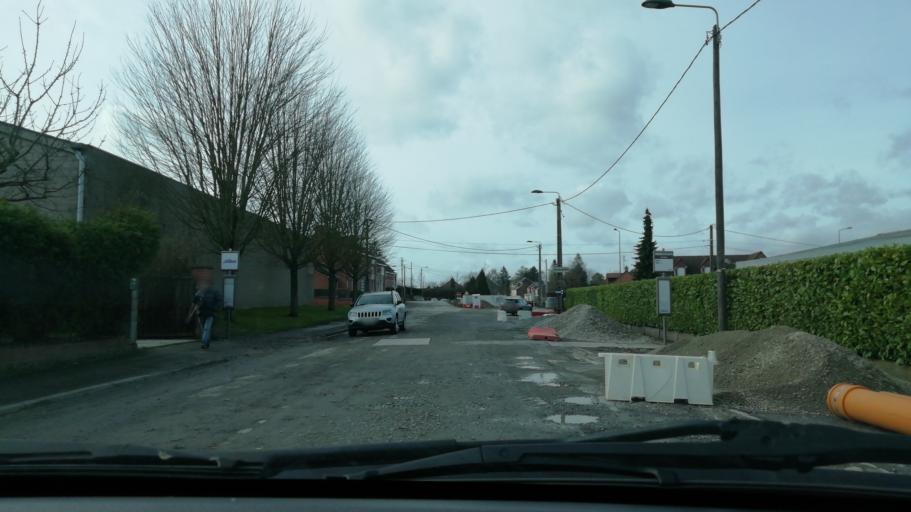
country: FR
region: Nord-Pas-de-Calais
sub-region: Departement du Nord
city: Louvroil
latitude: 50.2784
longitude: 3.9525
